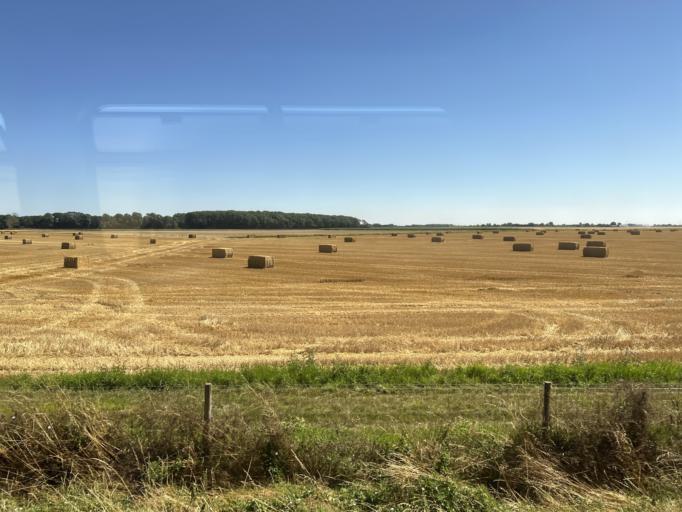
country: GB
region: England
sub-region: Lincolnshire
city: Spilsby
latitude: 53.1079
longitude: 0.1205
